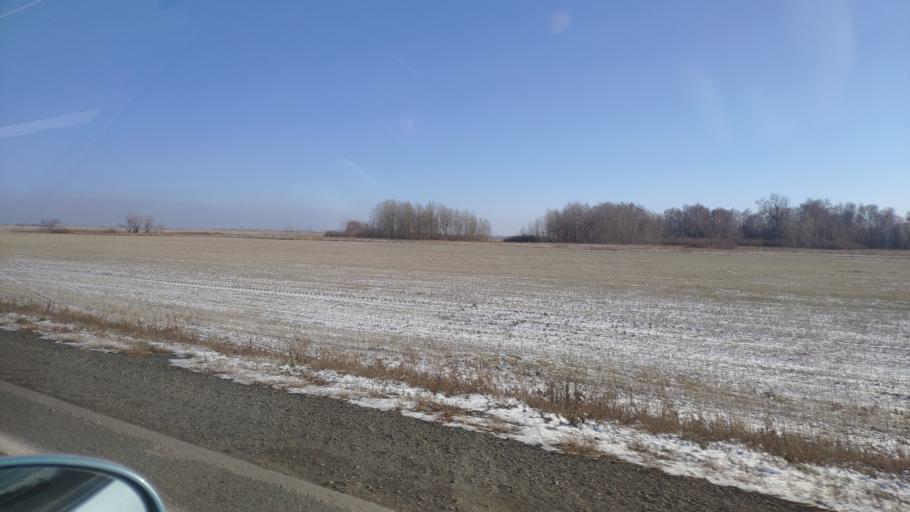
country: RU
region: Orenburg
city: Mednogorsk
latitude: 51.3240
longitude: 57.6065
